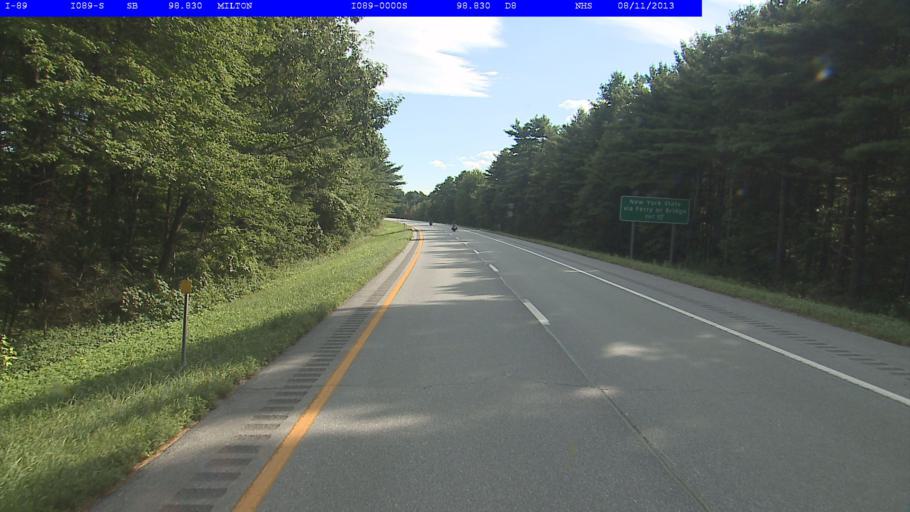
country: US
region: Vermont
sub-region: Chittenden County
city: Colchester
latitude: 44.6035
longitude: -73.1720
